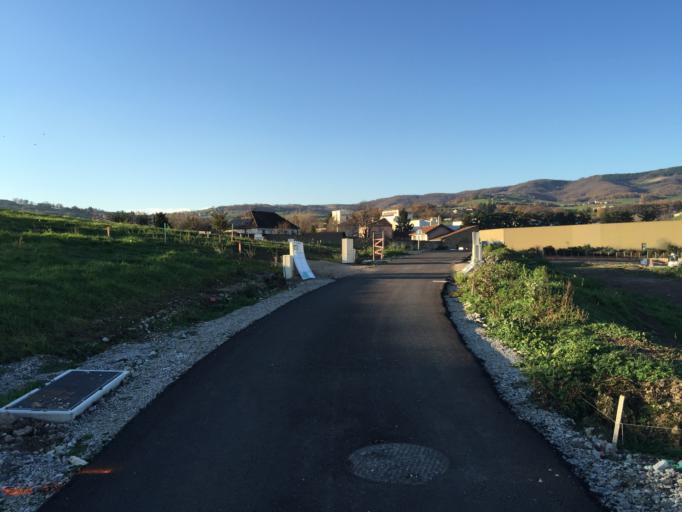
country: FR
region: Rhone-Alpes
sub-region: Departement de la Loire
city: Saint-Chamond
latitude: 45.4825
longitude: 4.5188
